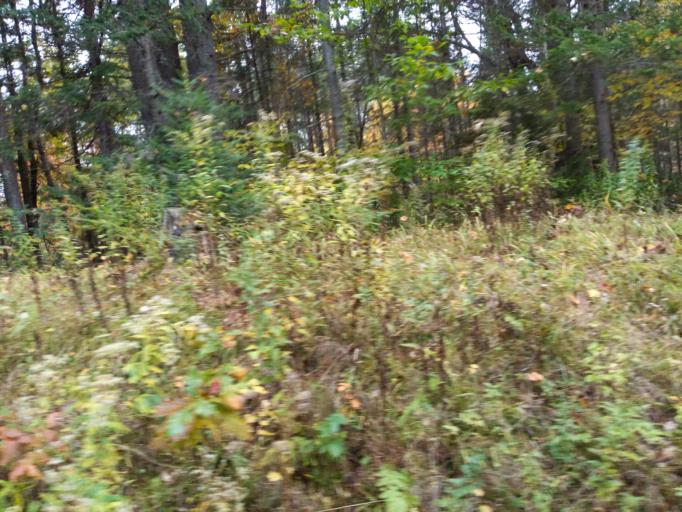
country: US
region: Maine
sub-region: Lincoln County
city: Wiscasset
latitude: 44.0801
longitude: -69.6235
